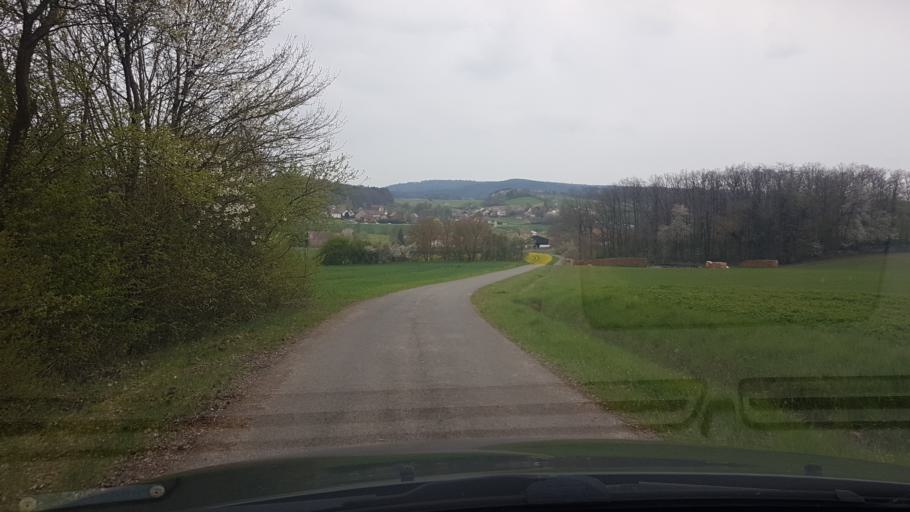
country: DE
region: Bavaria
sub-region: Upper Franconia
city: Gerach
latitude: 50.0475
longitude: 10.8233
